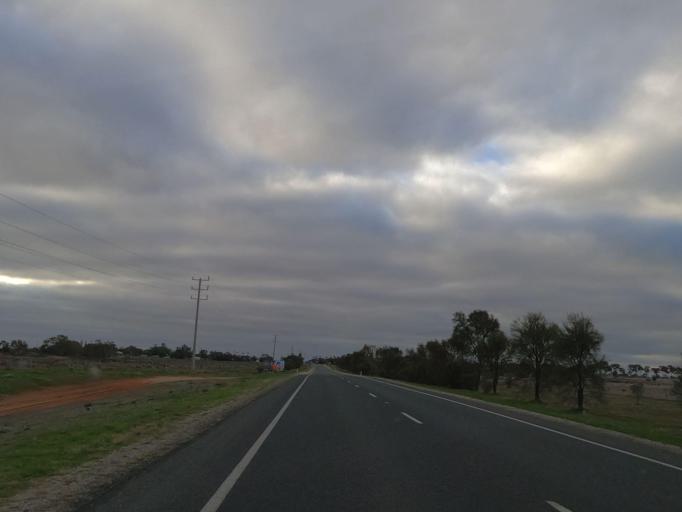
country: AU
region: Victoria
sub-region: Swan Hill
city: Swan Hill
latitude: -35.6172
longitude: 143.8034
